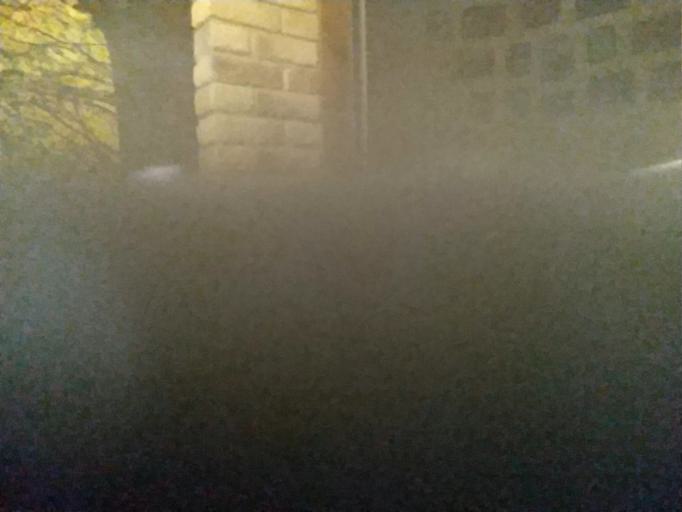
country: RU
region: Moskovskaya
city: Vysokovsk
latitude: 56.1655
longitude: 36.6360
